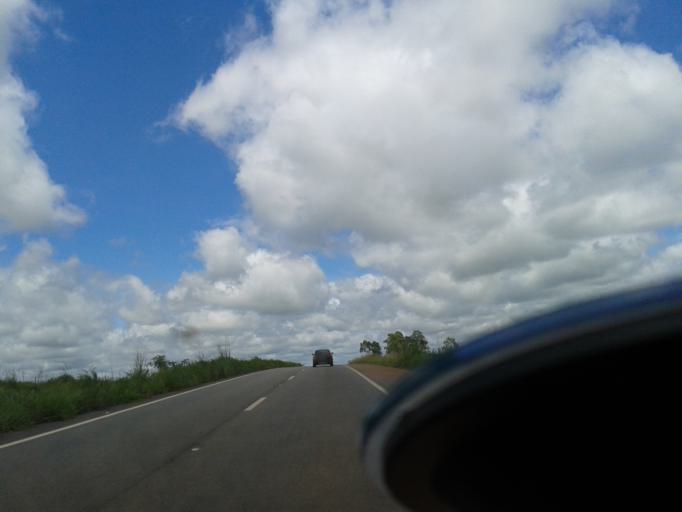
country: BR
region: Goias
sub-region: Itaberai
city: Itaberai
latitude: -16.1153
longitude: -49.6667
